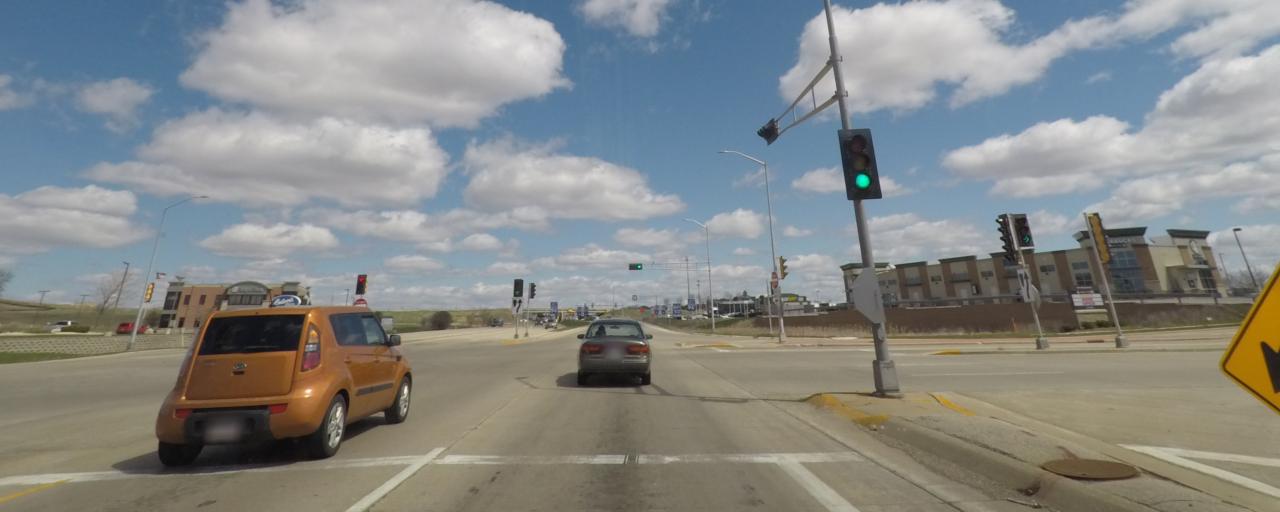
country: US
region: Wisconsin
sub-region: Jefferson County
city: Johnson Creek
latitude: 43.0824
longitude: -88.7633
